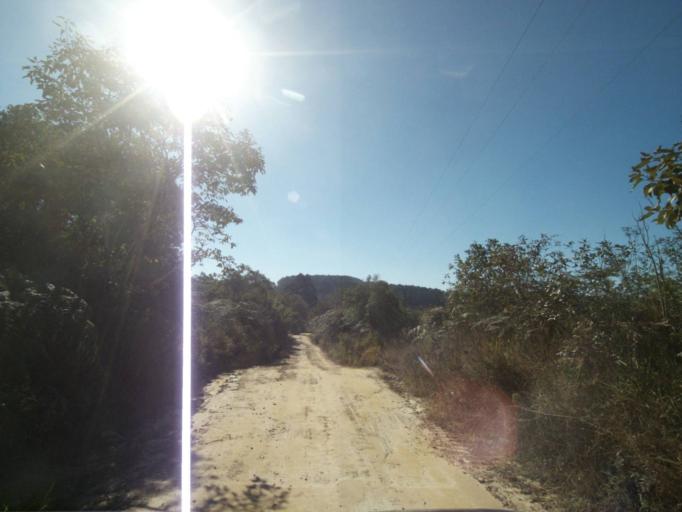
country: BR
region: Parana
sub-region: Tibagi
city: Tibagi
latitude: -24.5652
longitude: -50.4710
